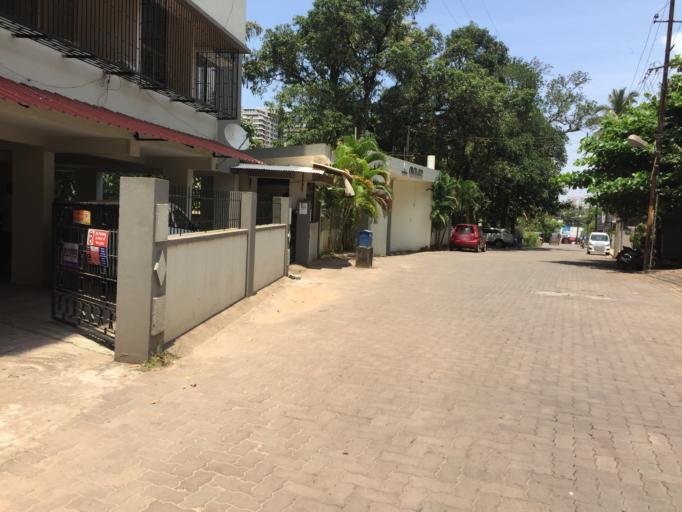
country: IN
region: Karnataka
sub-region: Dakshina Kannada
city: Mangalore
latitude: 12.8767
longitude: 74.8516
